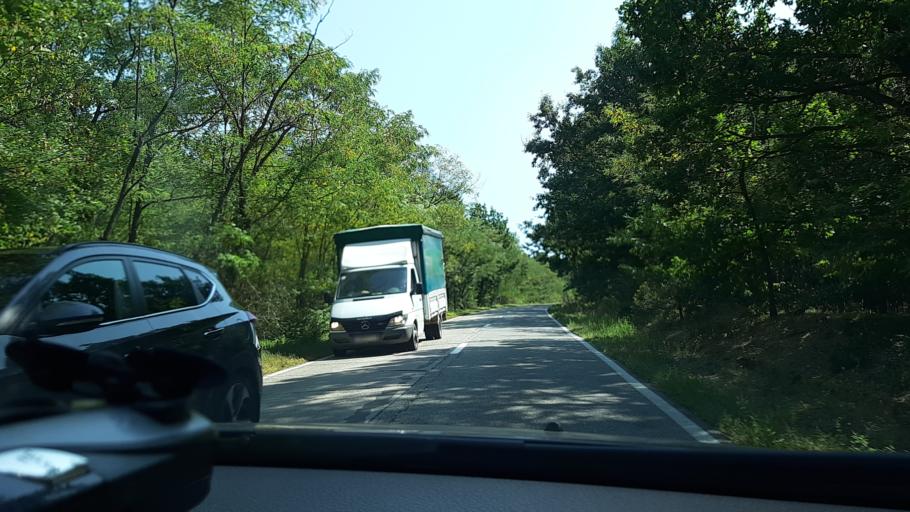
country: RO
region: Gorj
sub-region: Comuna Targu Carbunesti
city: Targu Carbunesti
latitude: 44.9490
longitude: 23.5612
